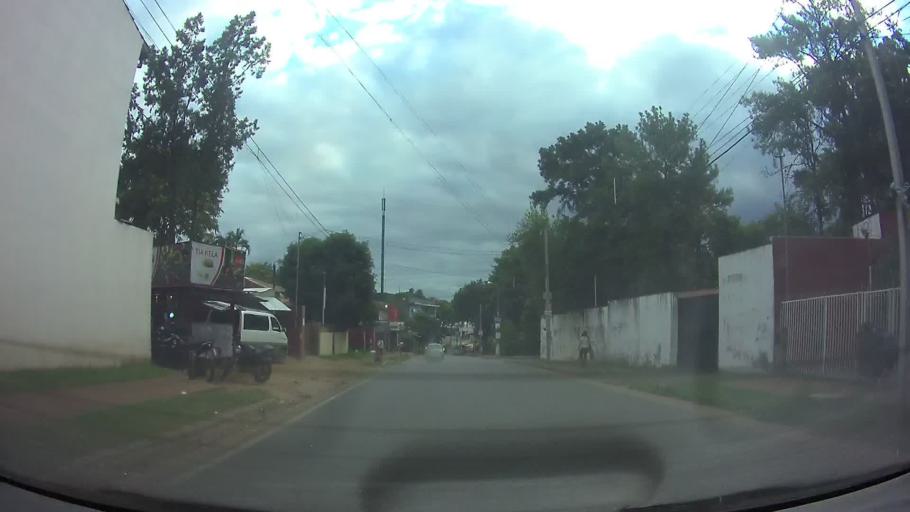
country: PY
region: Central
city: Fernando de la Mora
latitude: -25.3073
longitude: -57.5269
